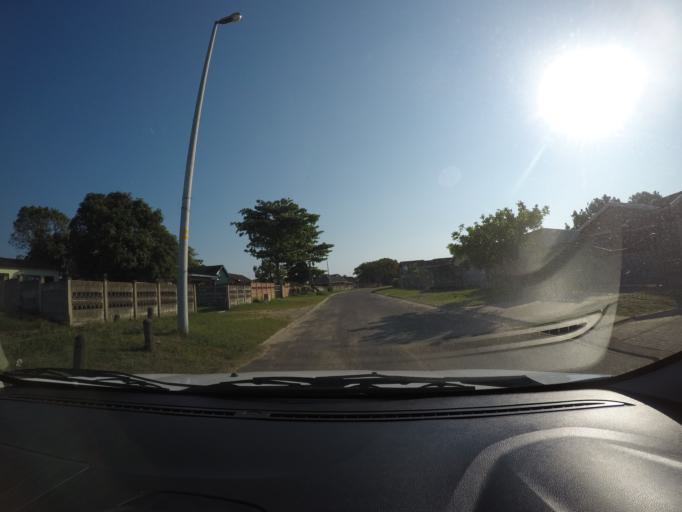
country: ZA
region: KwaZulu-Natal
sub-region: uThungulu District Municipality
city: Richards Bay
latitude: -28.7143
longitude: 32.0373
